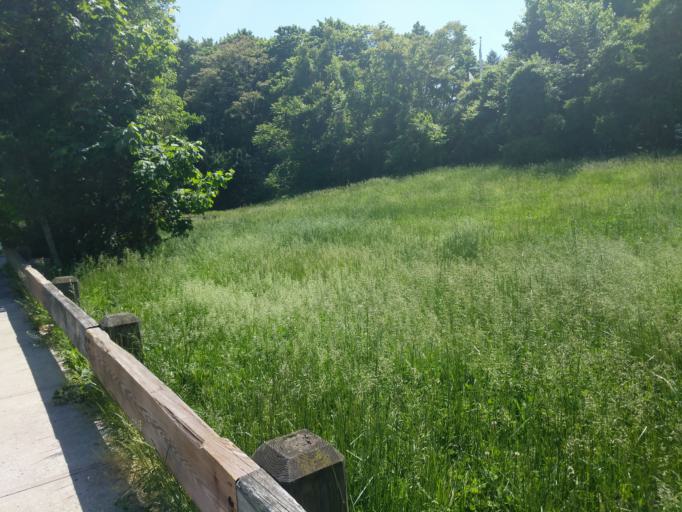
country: US
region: New Jersey
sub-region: Hudson County
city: Bayonne
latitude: 40.6396
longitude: -74.0892
